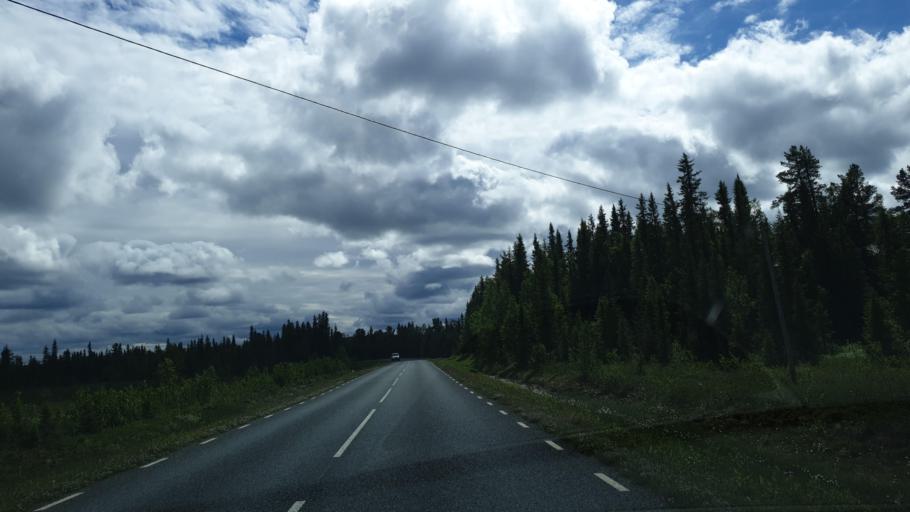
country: SE
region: Vaesterbotten
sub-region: Vilhelmina Kommun
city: Sjoberg
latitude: 65.2452
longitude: 15.7468
